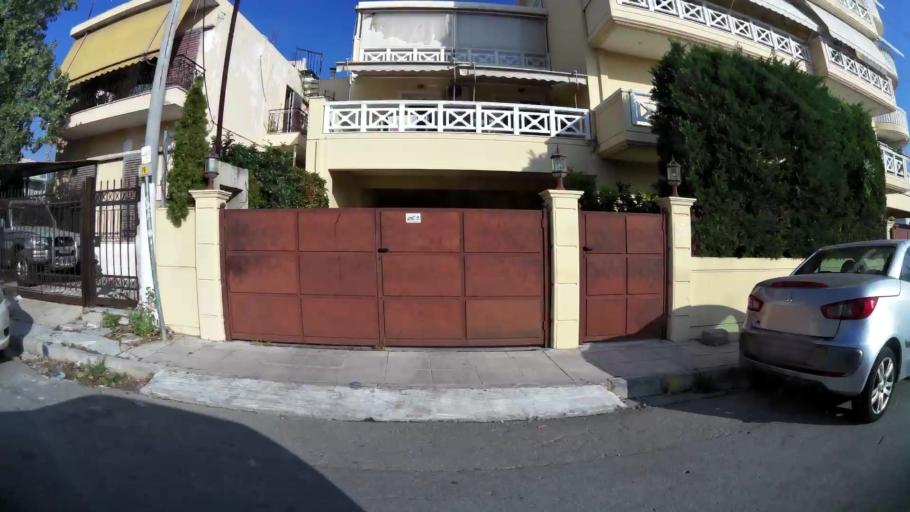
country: GR
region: Attica
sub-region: Nomarchia Anatolikis Attikis
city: Acharnes
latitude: 38.0751
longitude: 23.7329
